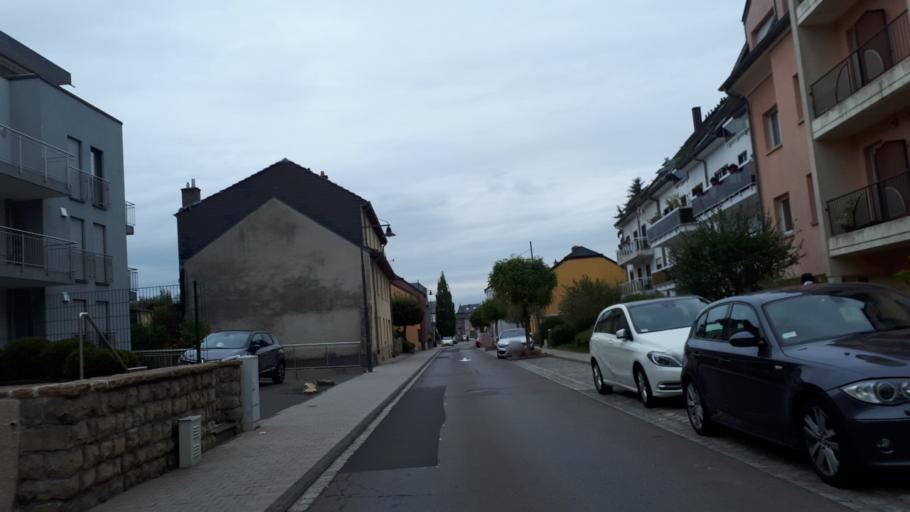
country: LU
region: Luxembourg
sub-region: Canton de Luxembourg
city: Strassen
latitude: 49.6188
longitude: 6.0665
